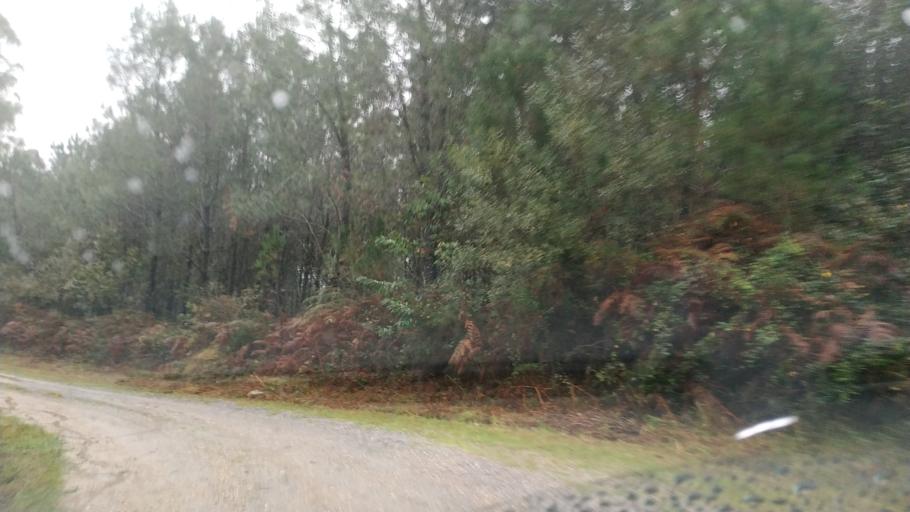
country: ES
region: Galicia
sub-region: Provincia da Coruna
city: Negreira
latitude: 42.9069
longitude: -8.7646
